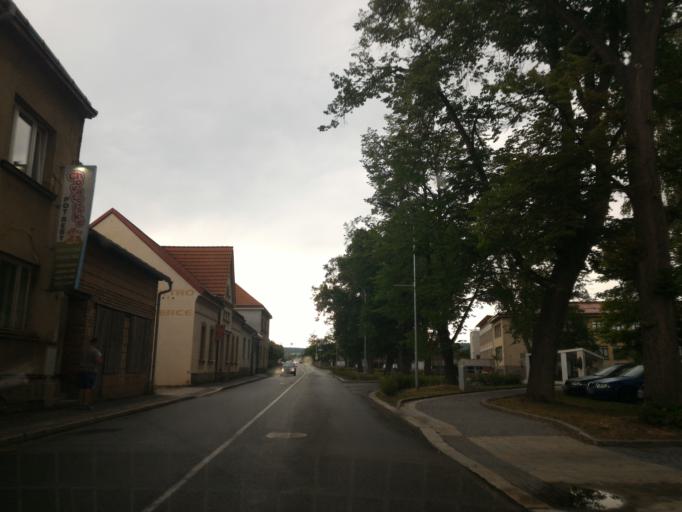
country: CZ
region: Vysocina
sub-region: Okres Jihlava
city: Telc
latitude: 49.1821
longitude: 15.4496
